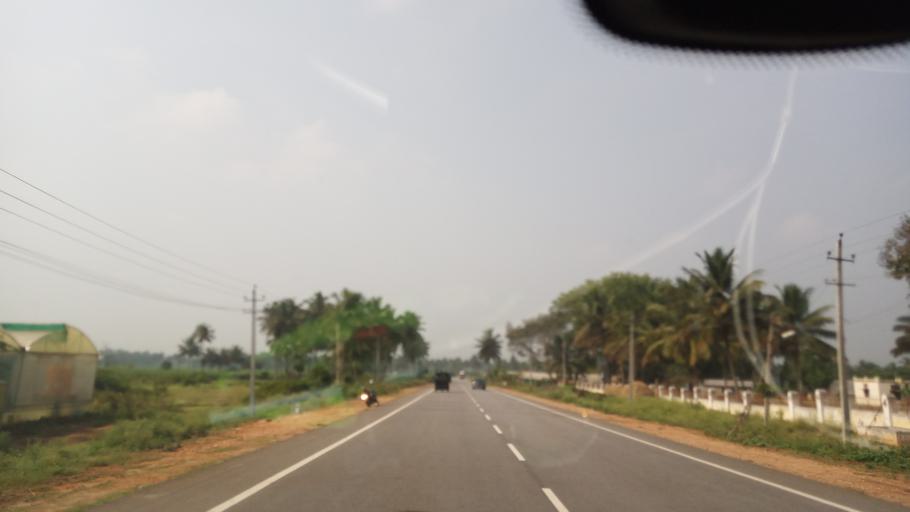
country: IN
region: Karnataka
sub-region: Mandya
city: Pandavapura
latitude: 12.5473
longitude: 76.6713
